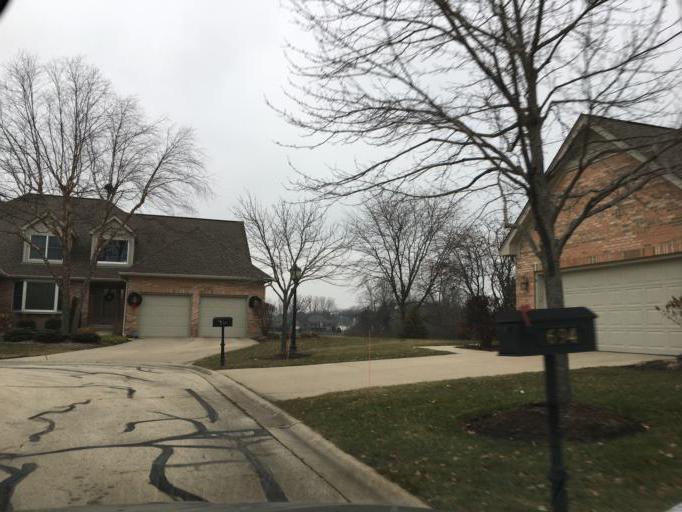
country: US
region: Illinois
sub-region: McHenry County
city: Lakewood
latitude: 42.2219
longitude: -88.3611
